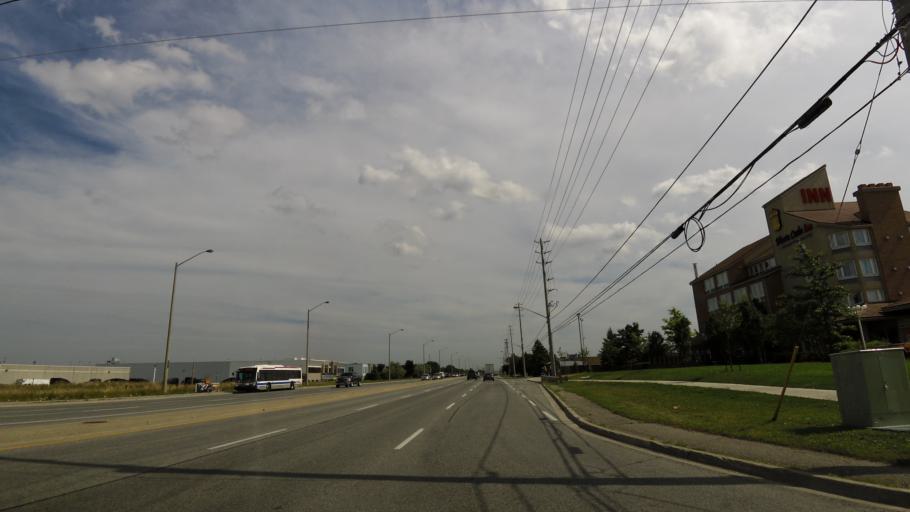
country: CA
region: Ontario
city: Brampton
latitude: 43.7408
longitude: -79.6923
